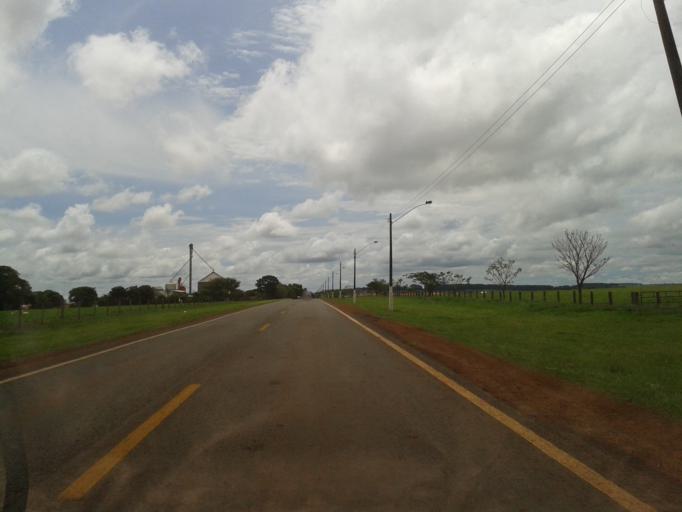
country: BR
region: Goias
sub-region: Buriti Alegre
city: Buriti Alegre
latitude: -18.1347
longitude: -49.0226
